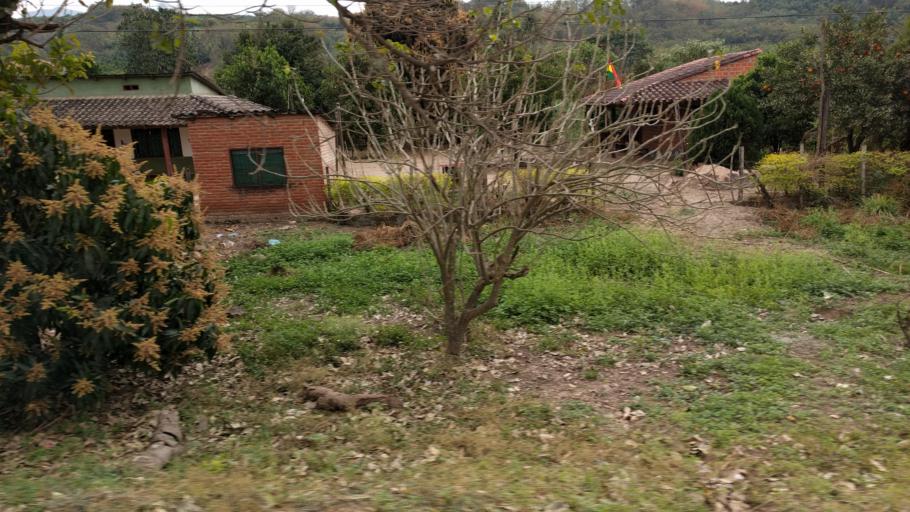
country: BO
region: Santa Cruz
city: Jorochito
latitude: -18.1552
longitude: -63.4969
